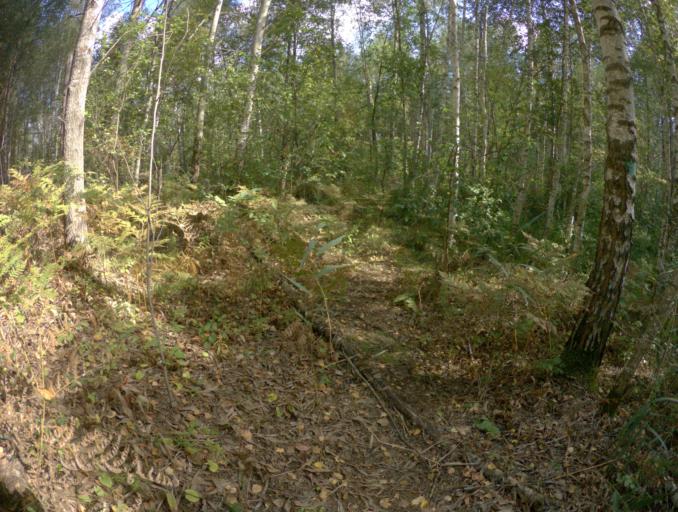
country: RU
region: Vladimir
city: Pokrov
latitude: 55.8456
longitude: 39.2393
